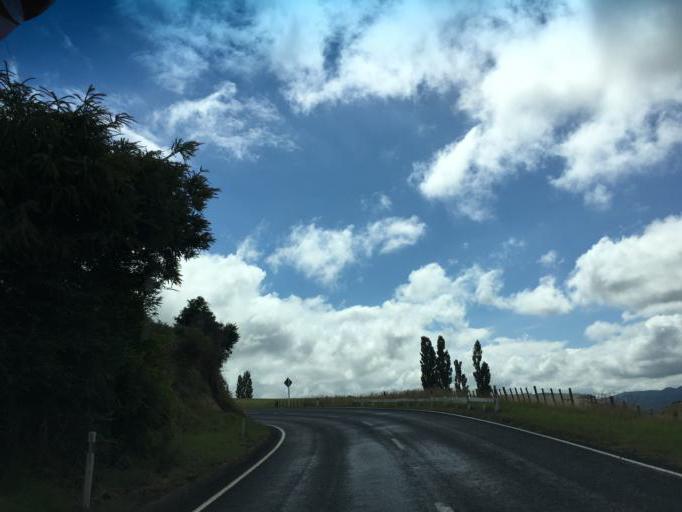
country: NZ
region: Hawke's Bay
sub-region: Napier City
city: Napier
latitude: -39.1330
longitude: 177.0025
